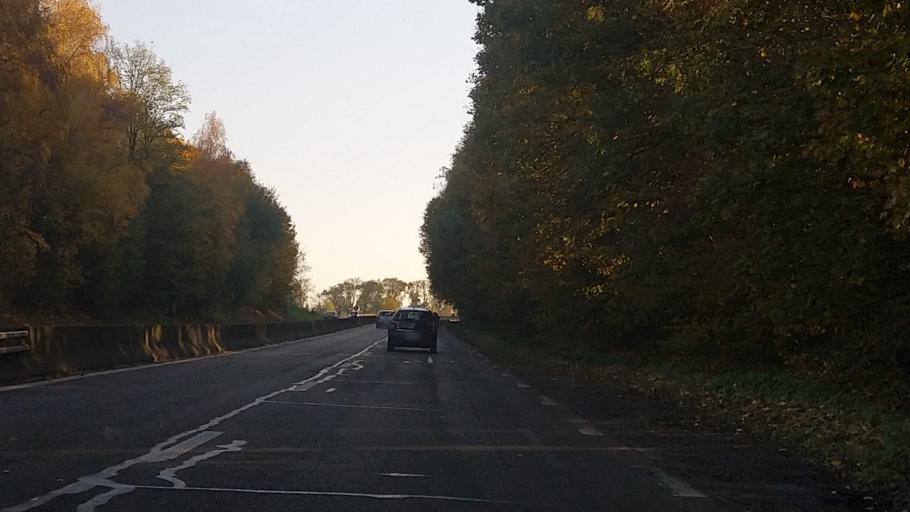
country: FR
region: Ile-de-France
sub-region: Departement du Val-d'Oise
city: Ezanville
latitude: 49.0248
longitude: 2.3489
